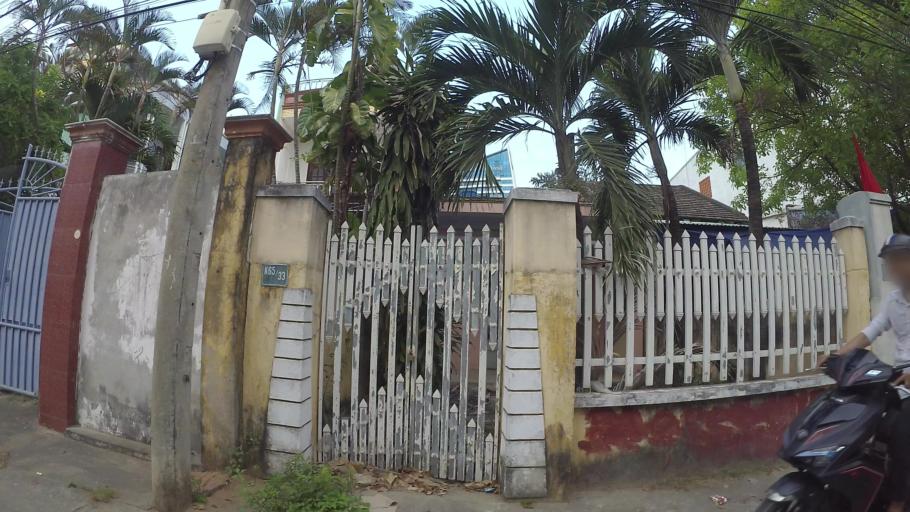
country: VN
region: Da Nang
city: Son Tra
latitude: 16.0613
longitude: 108.2439
